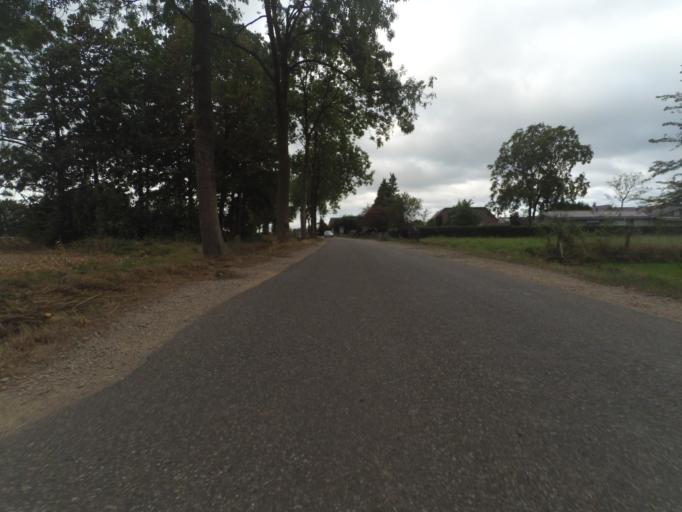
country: NL
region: Gelderland
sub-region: Gemeente Buren
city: Lienden
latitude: 51.9618
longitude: 5.4967
